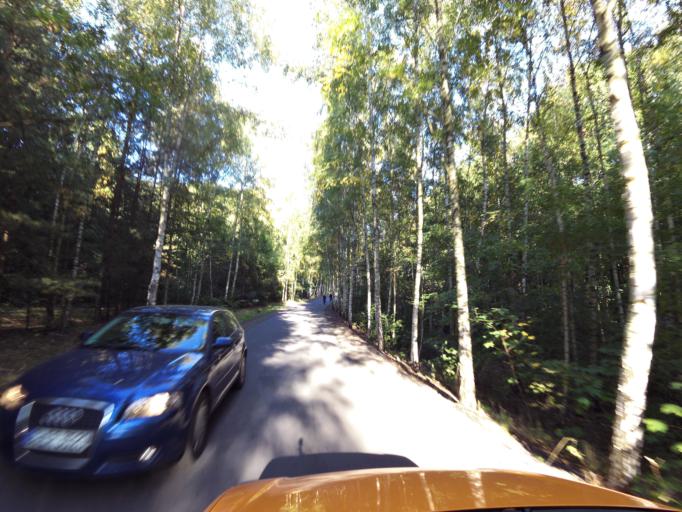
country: DE
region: Berlin
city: Kladow
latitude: 52.4384
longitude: 13.1098
